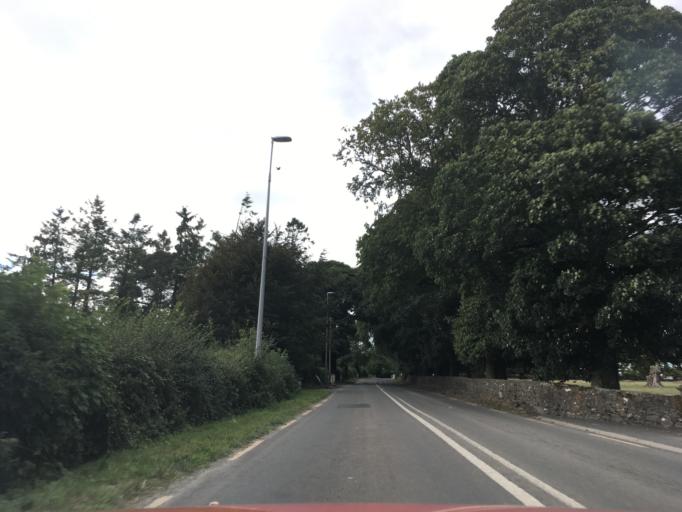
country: IE
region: Munster
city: Cahir
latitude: 52.4366
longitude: -7.8839
